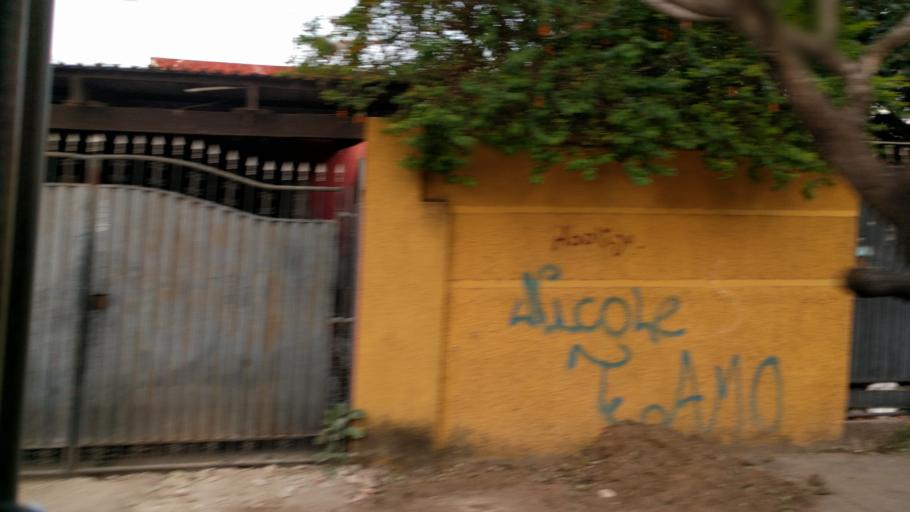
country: BO
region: Santa Cruz
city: Santa Cruz de la Sierra
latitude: -17.7819
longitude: -63.1919
